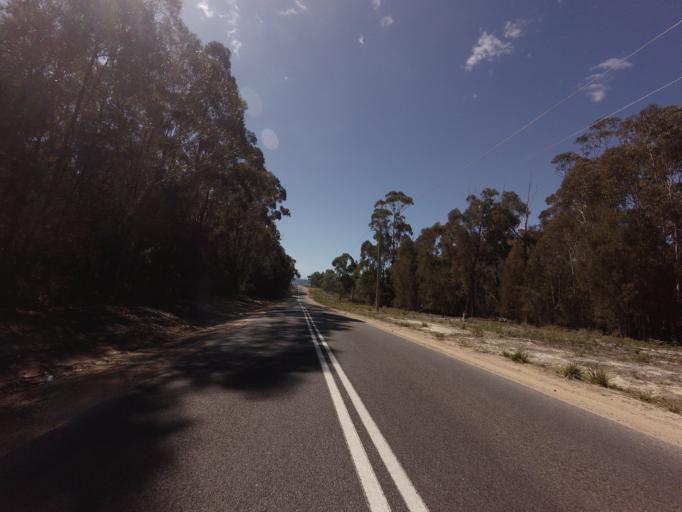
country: AU
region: Tasmania
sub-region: Break O'Day
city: St Helens
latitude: -41.6715
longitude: 148.2807
